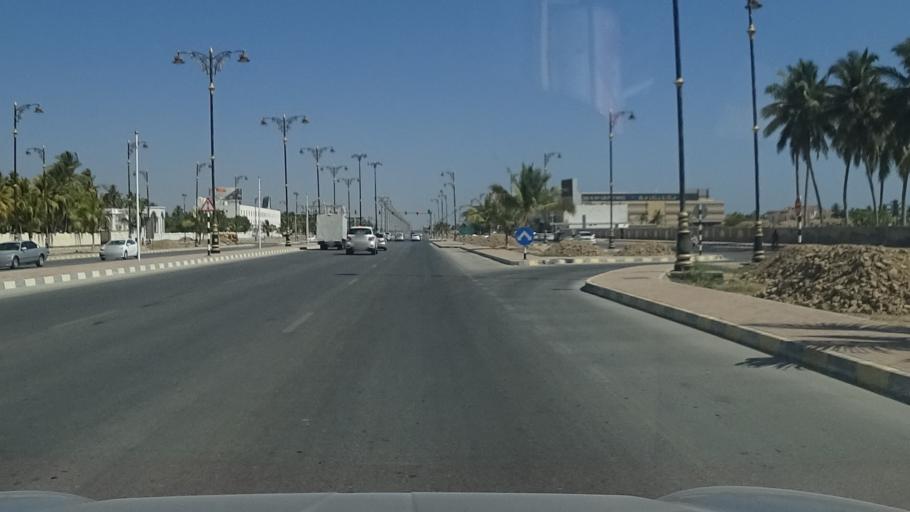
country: OM
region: Zufar
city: Salalah
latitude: 17.0362
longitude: 54.1582
